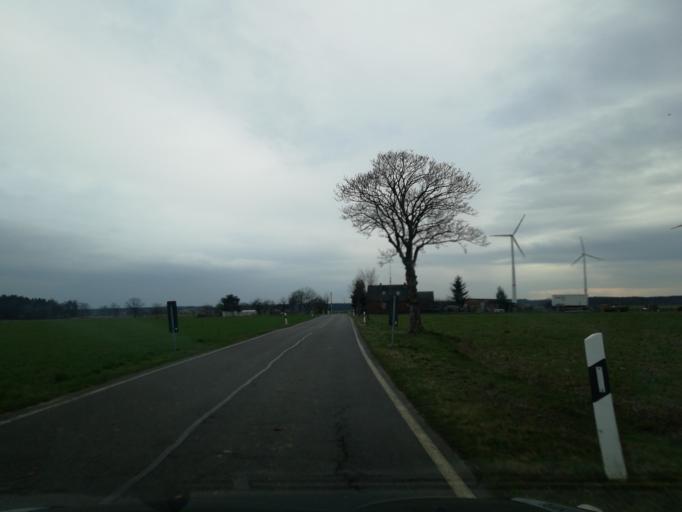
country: DE
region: Brandenburg
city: Vetschau
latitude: 51.7434
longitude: 14.0266
